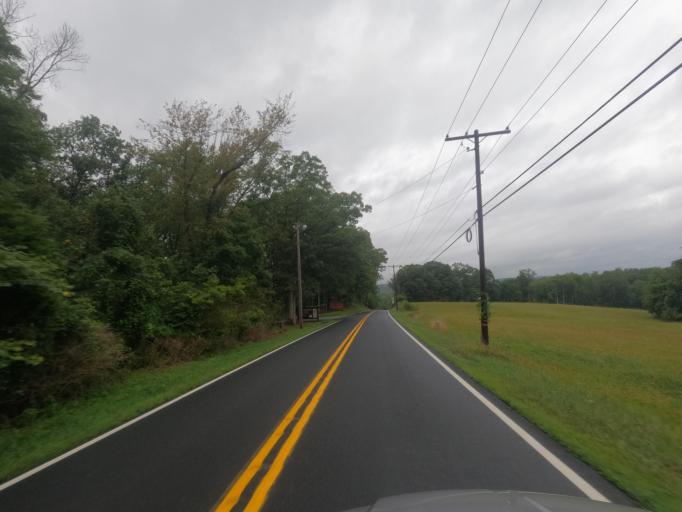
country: US
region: West Virginia
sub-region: Berkeley County
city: Martinsburg
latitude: 39.6180
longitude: -78.0020
